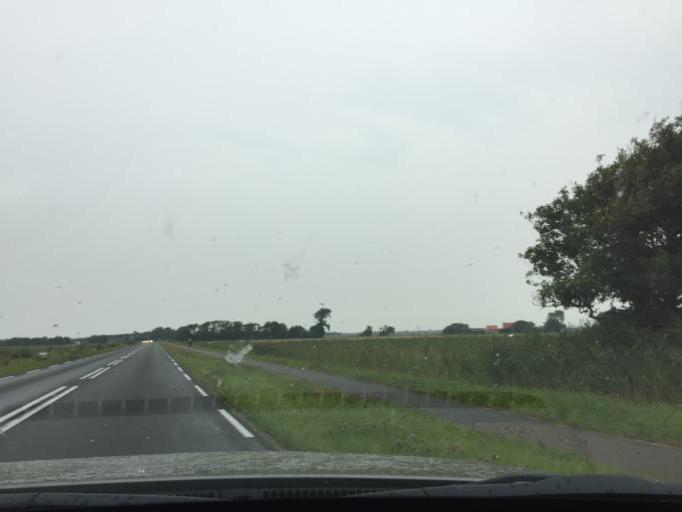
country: NL
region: North Holland
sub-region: Gemeente Texel
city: Den Burg
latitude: 53.0646
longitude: 4.7761
